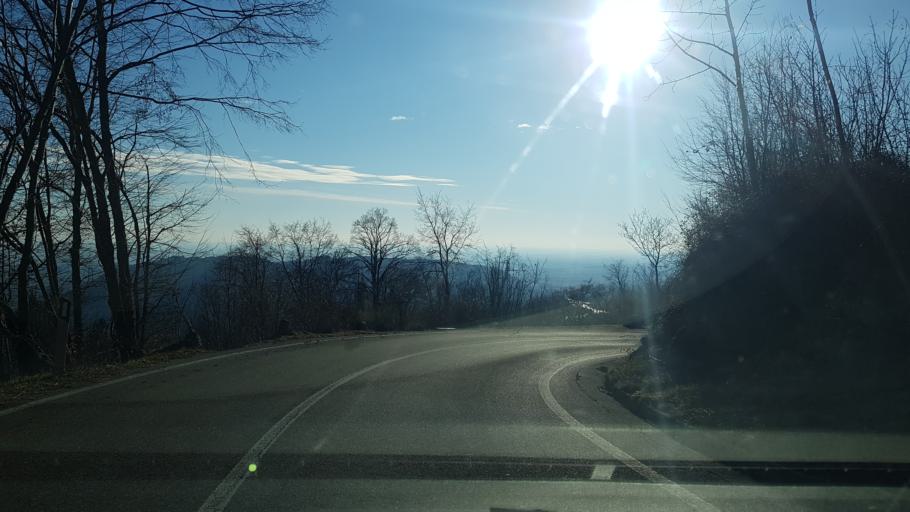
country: IT
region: Friuli Venezia Giulia
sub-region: Provincia di Udine
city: Forgaria nel Friuli
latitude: 46.2334
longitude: 12.9924
